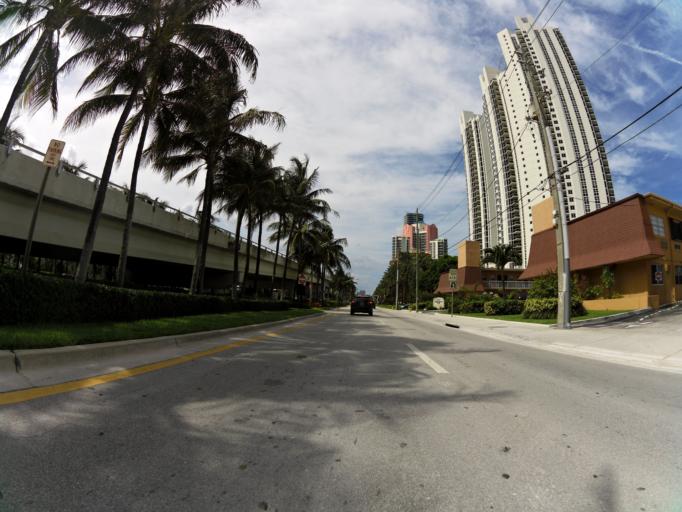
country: US
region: Florida
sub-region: Miami-Dade County
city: Sunny Isles Beach
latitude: 25.9522
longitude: -80.1205
